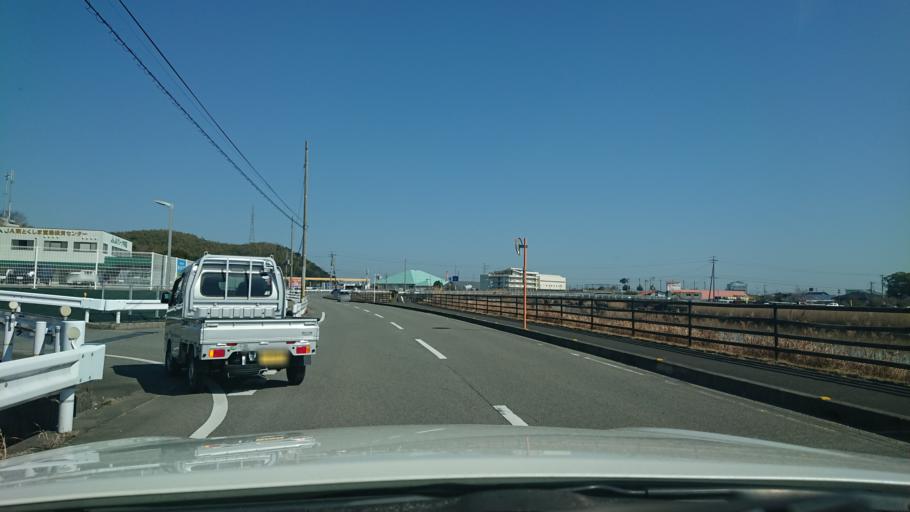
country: JP
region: Tokushima
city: Komatsushimacho
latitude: 33.9751
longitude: 134.6030
